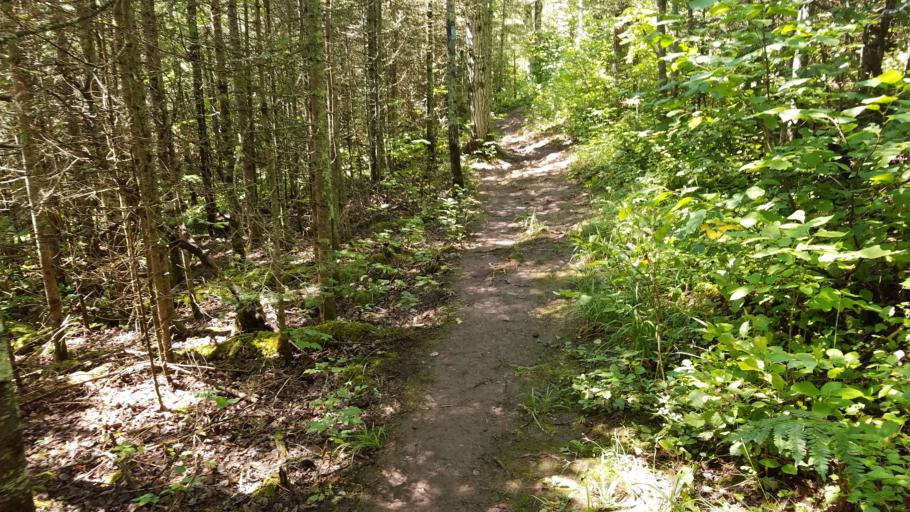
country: US
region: Michigan
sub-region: Ontonagon County
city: Ontonagon
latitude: 46.6516
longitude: -89.1595
